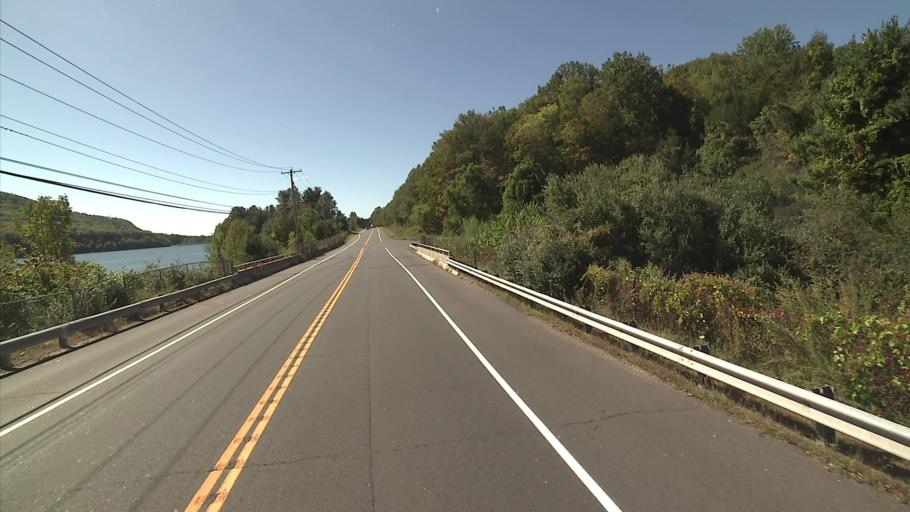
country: US
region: Connecticut
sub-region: New Haven County
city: Woodbridge
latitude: 41.3774
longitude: -72.9766
